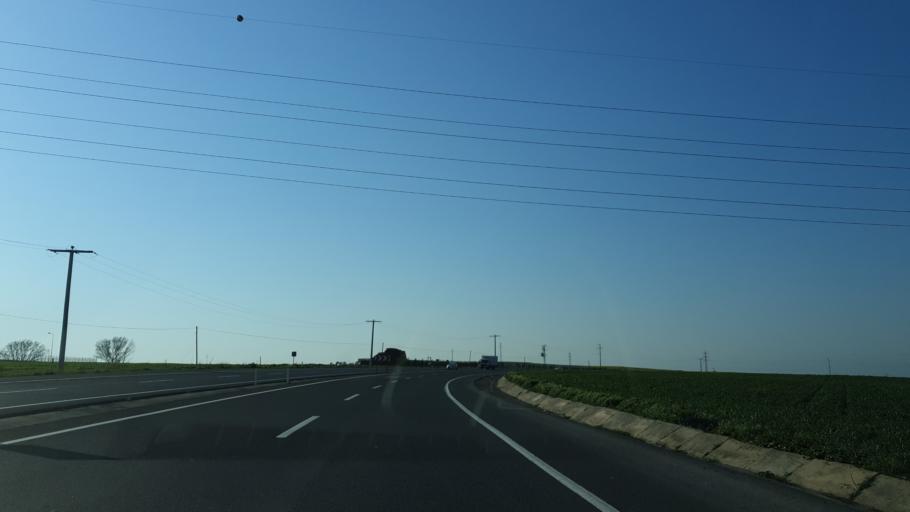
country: TR
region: Tekirdag
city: Corlu
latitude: 41.1032
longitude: 27.7538
